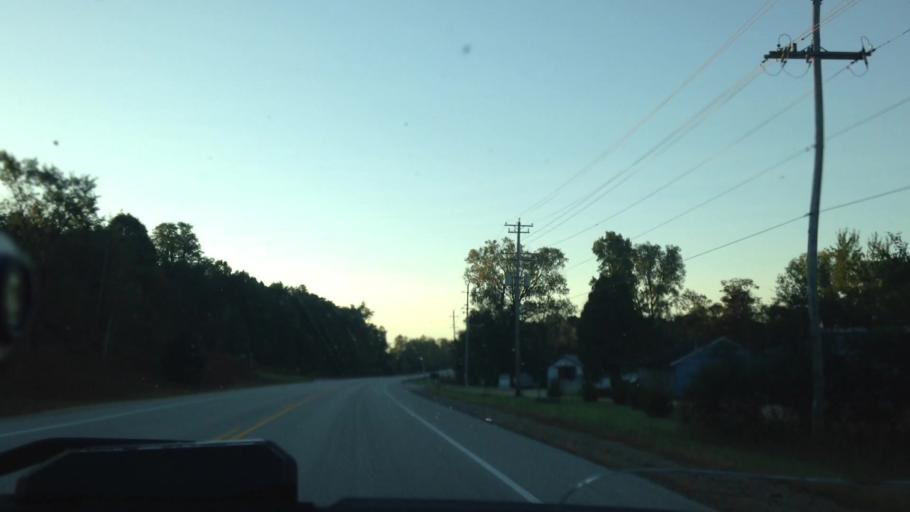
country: US
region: Wisconsin
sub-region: Washington County
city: Newburg
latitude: 43.4248
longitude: -88.0326
